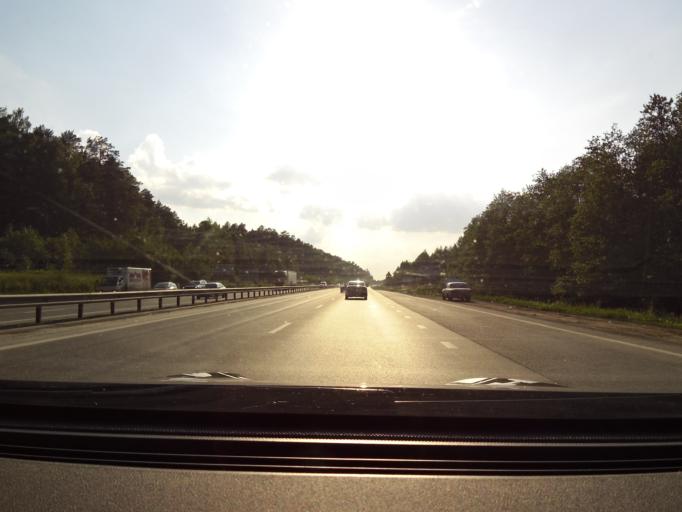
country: RU
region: Sverdlovsk
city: Severka
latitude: 56.8334
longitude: 60.3128
